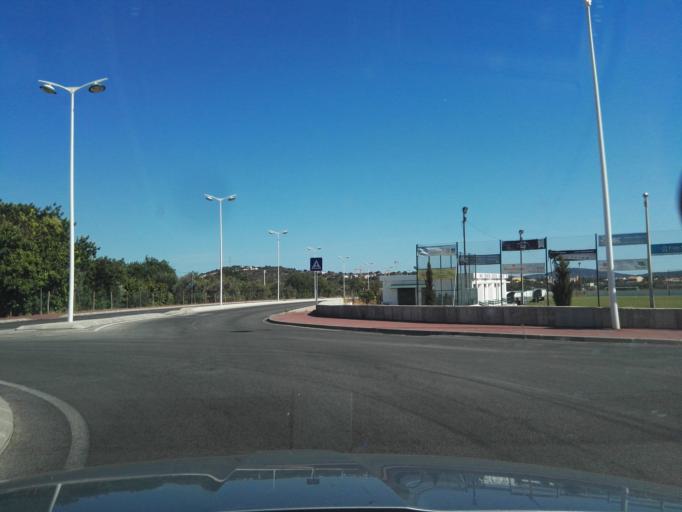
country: PT
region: Faro
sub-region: Sao Bras de Alportel
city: Sao Bras de Alportel
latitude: 37.1580
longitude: -7.8805
